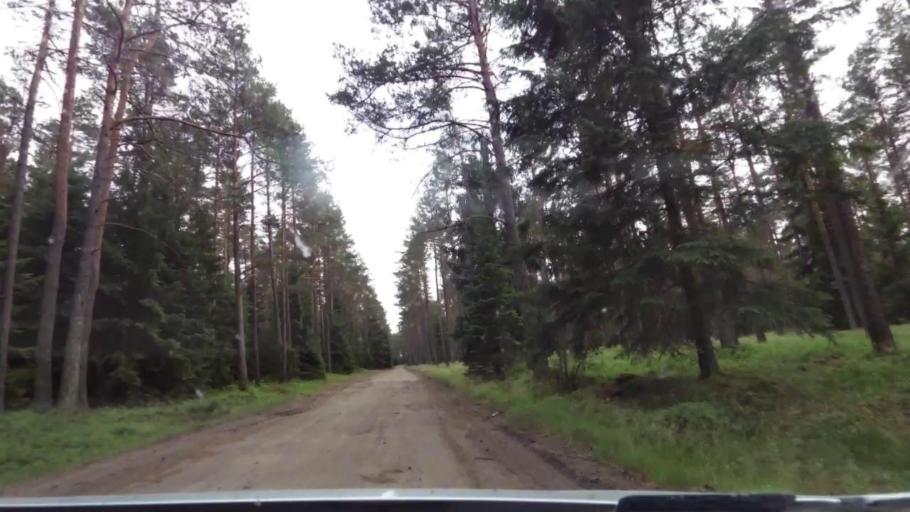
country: PL
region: Pomeranian Voivodeship
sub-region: Powiat bytowski
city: Trzebielino
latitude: 54.2132
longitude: 17.0042
